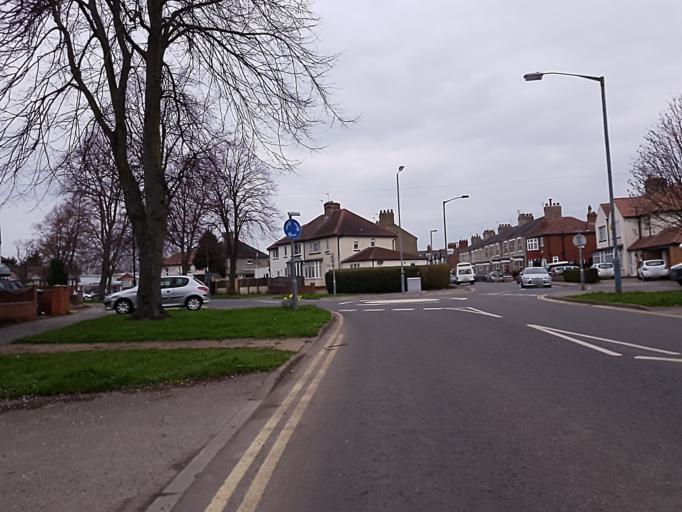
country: GB
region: England
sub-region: City of York
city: York
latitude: 53.9632
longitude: -1.0666
